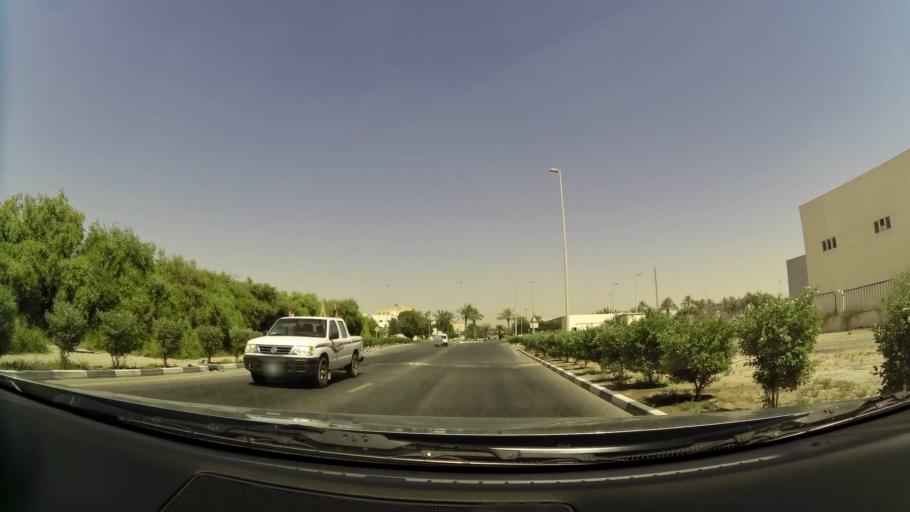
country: AE
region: Dubai
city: Dubai
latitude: 24.9734
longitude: 55.1622
